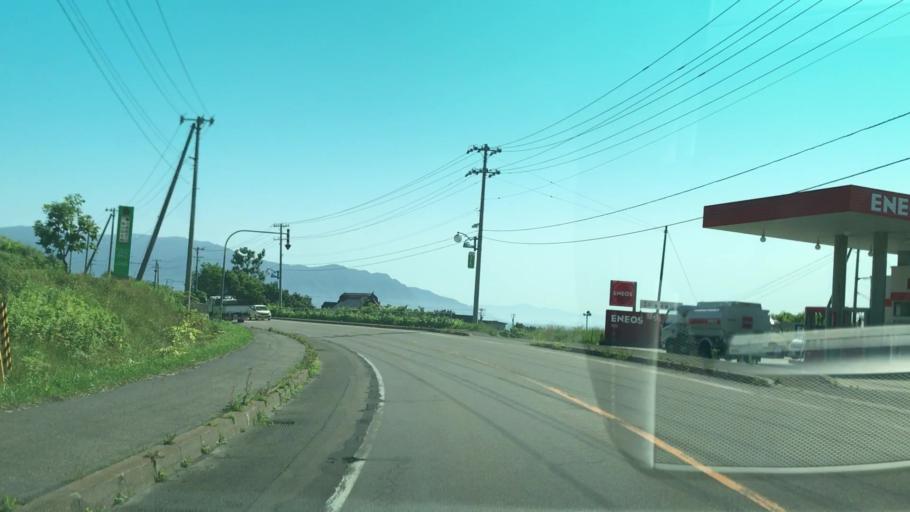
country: JP
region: Hokkaido
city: Iwanai
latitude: 43.0623
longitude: 140.4975
